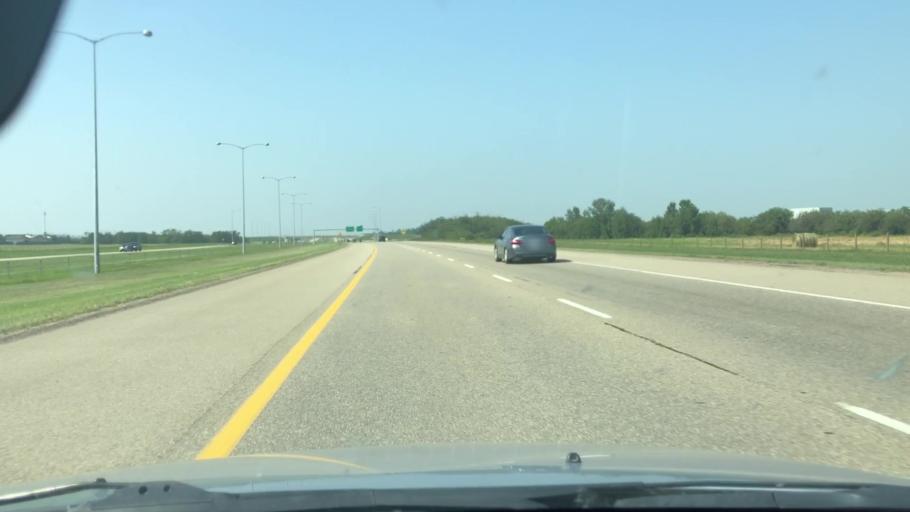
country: CA
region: Alberta
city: St. Albert
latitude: 53.6444
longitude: -113.5283
